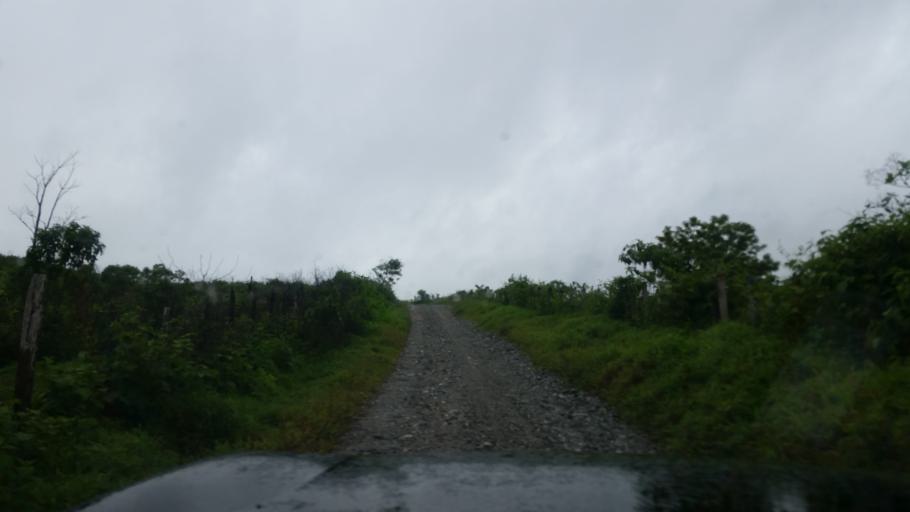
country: NI
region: Atlantico Norte (RAAN)
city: Bonanza
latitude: 14.0810
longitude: -84.6759
